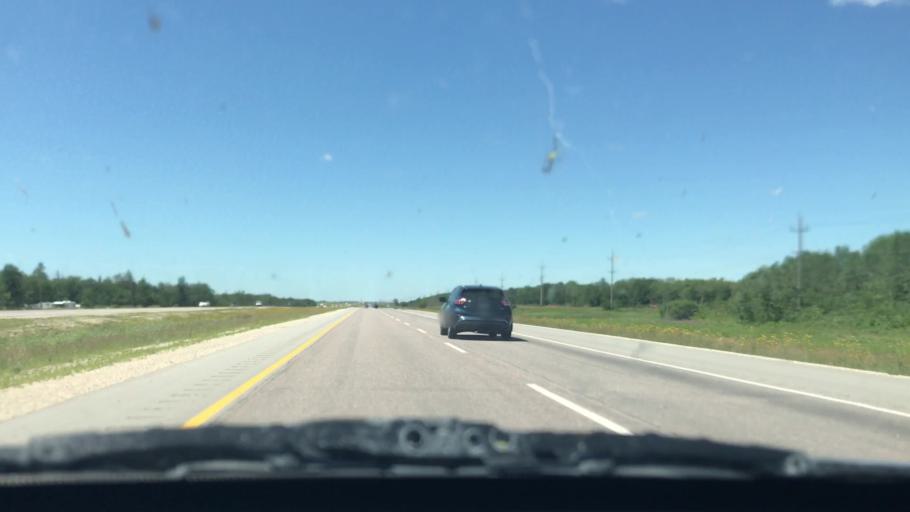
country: CA
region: Manitoba
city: Steinbach
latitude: 49.6808
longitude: -96.5950
